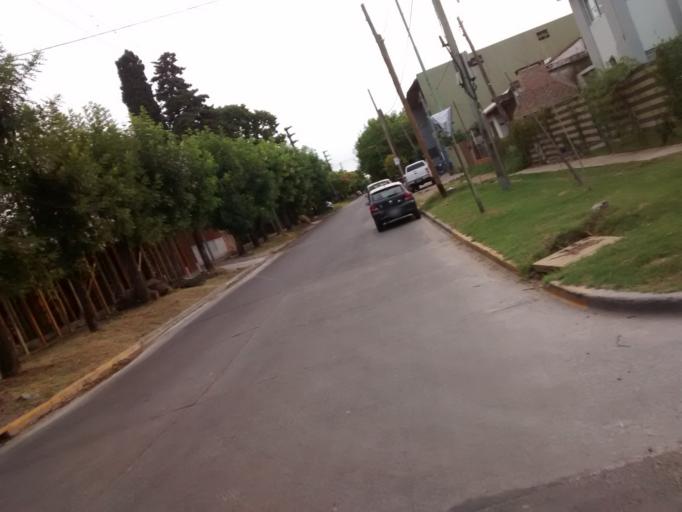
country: AR
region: Buenos Aires
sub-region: Partido de La Plata
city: La Plata
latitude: -34.8755
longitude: -58.0605
